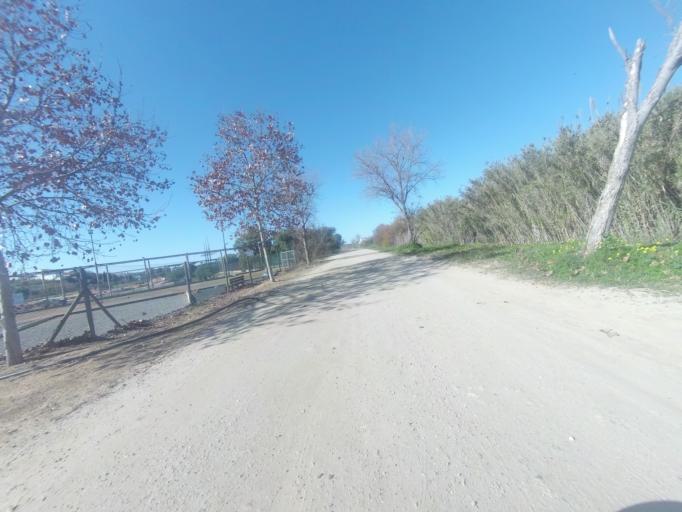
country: ES
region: Andalusia
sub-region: Provincia de Huelva
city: Palos de la Frontera
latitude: 37.2333
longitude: -6.8919
